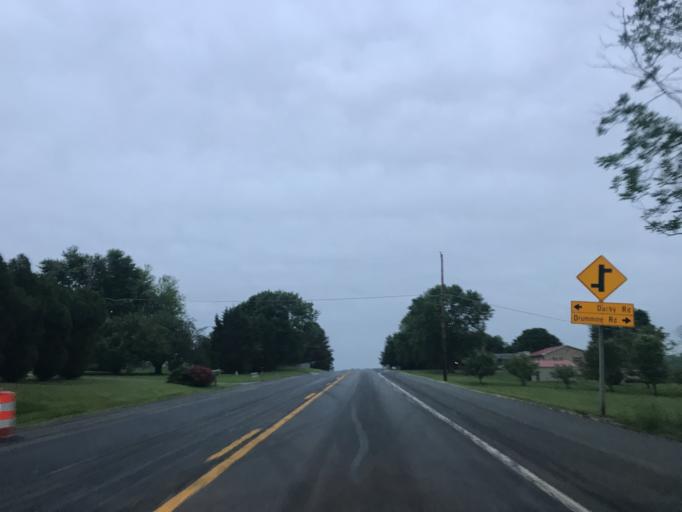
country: US
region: Maryland
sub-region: Frederick County
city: Linganore
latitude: 39.4309
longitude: -77.2535
